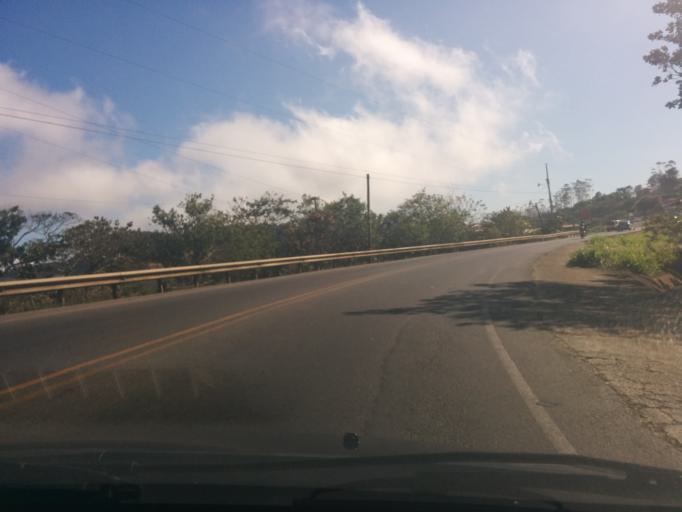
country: CR
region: Alajuela
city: San Rafael
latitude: 10.0588
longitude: -84.5020
